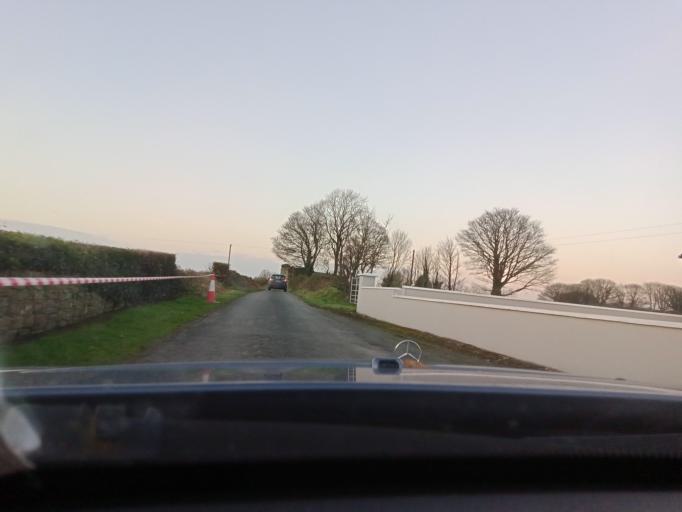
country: IE
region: Munster
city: Carrick-on-Suir
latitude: 52.4341
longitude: -7.3930
